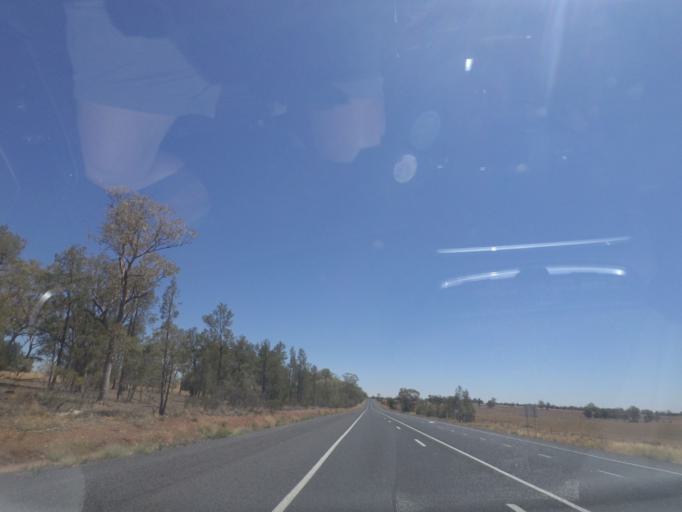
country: AU
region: New South Wales
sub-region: Gilgandra
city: Gilgandra
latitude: -31.4886
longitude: 148.8753
